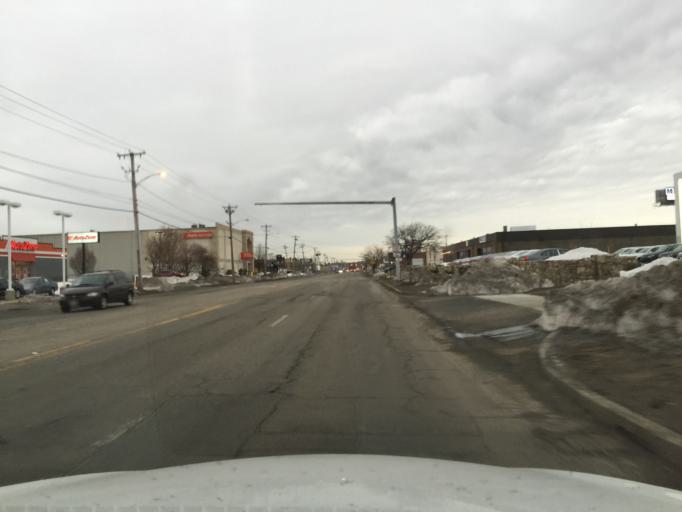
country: US
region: Massachusetts
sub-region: Middlesex County
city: Somerville
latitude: 42.4029
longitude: -71.0988
